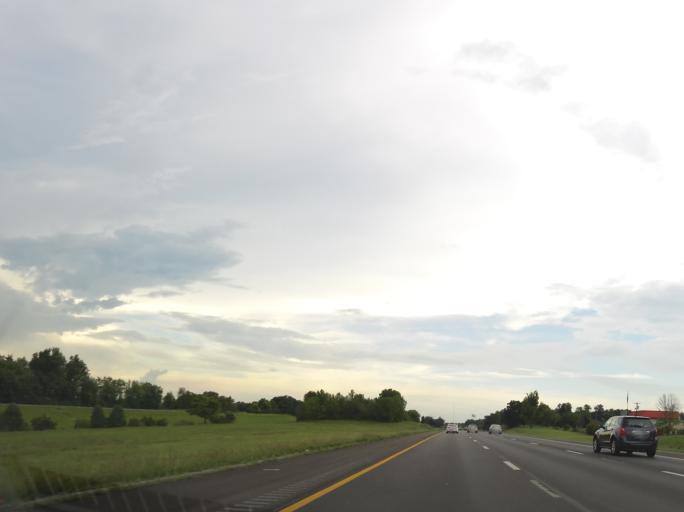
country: US
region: Kentucky
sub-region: Madison County
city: Richmond
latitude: 37.8192
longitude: -84.3232
